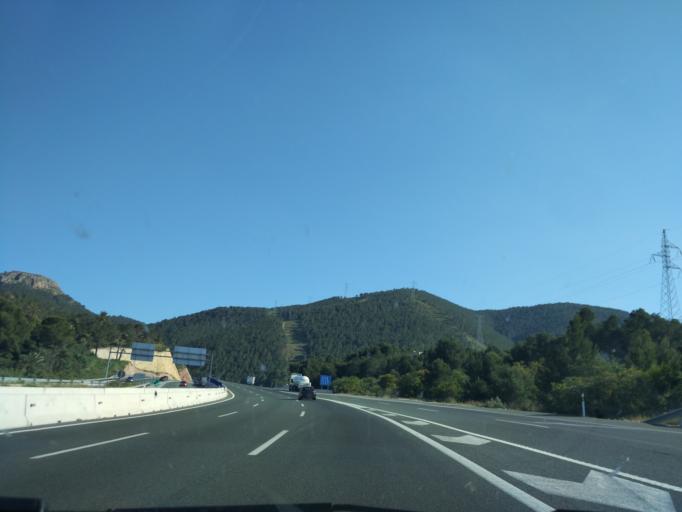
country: ES
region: Murcia
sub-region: Murcia
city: Alcantarilla
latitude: 37.9138
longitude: -1.1651
